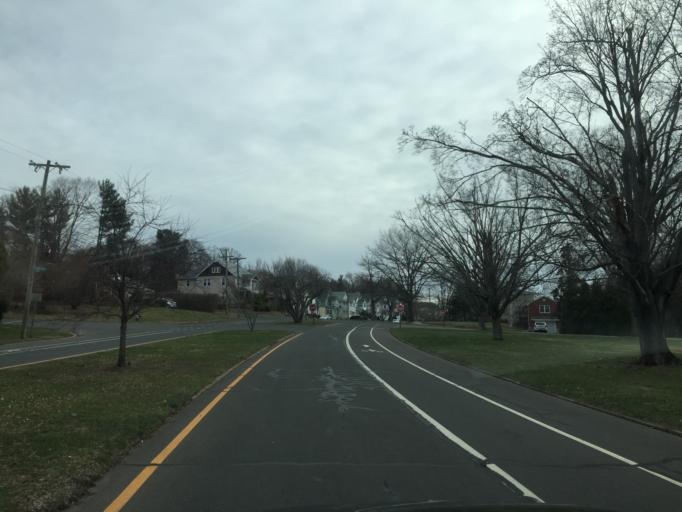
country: US
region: Connecticut
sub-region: Hartford County
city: New Britain
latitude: 41.6865
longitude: -72.7838
